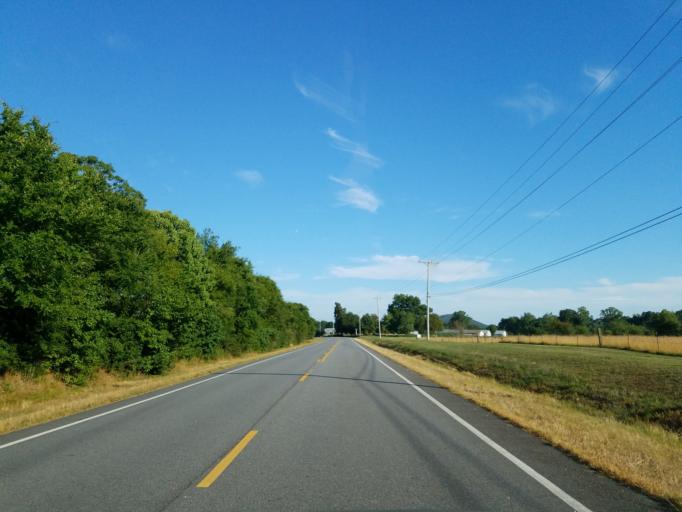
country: US
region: Georgia
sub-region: Gordon County
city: Calhoun
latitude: 34.5919
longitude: -85.0383
